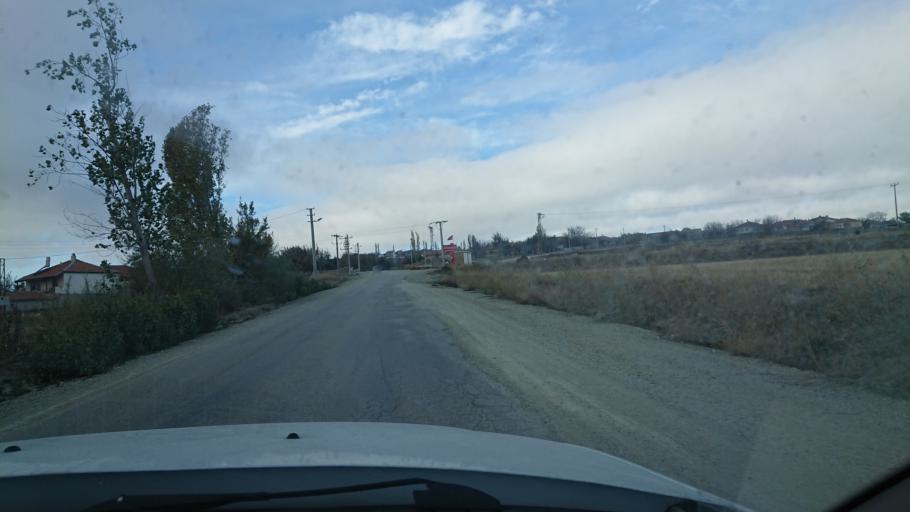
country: TR
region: Aksaray
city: Ortakoy
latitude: 38.7556
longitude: 34.0158
